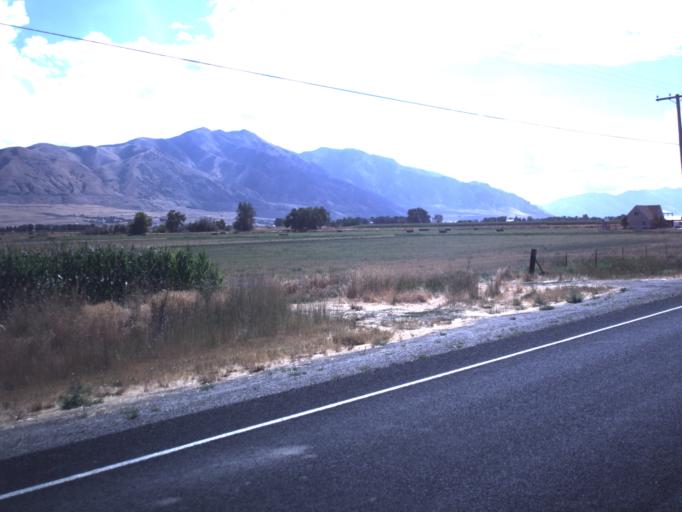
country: US
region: Utah
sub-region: Box Elder County
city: Garland
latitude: 41.7661
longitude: -112.1488
